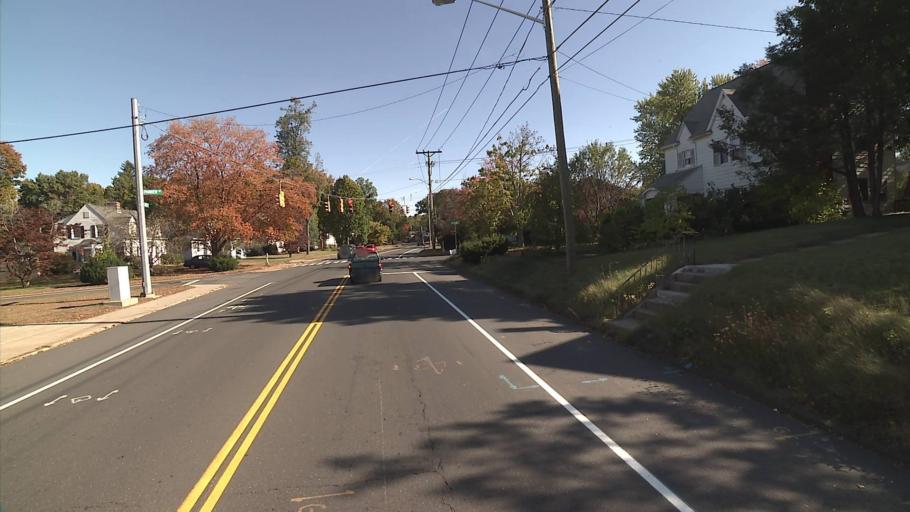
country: US
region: Connecticut
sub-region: Hartford County
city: Manchester
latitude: 41.7790
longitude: -72.5058
